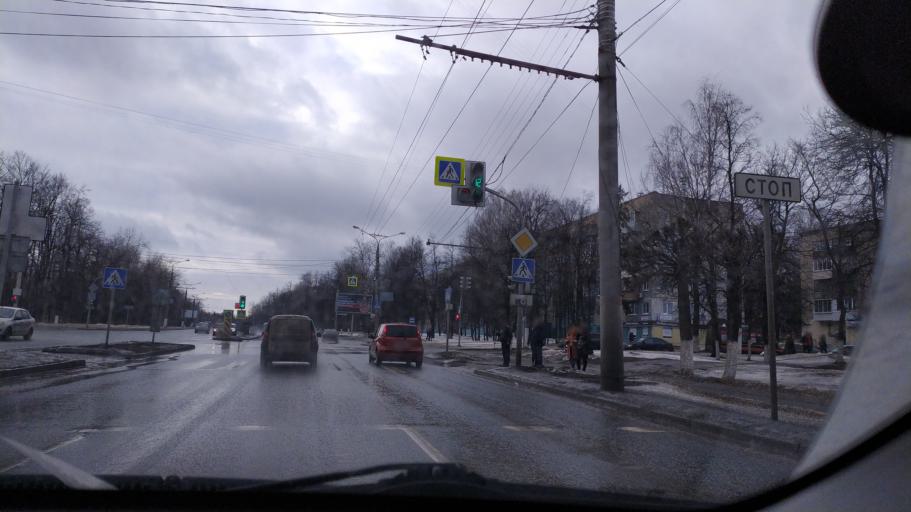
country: RU
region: Chuvashia
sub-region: Cheboksarskiy Rayon
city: Cheboksary
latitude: 56.1412
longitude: 47.1989
